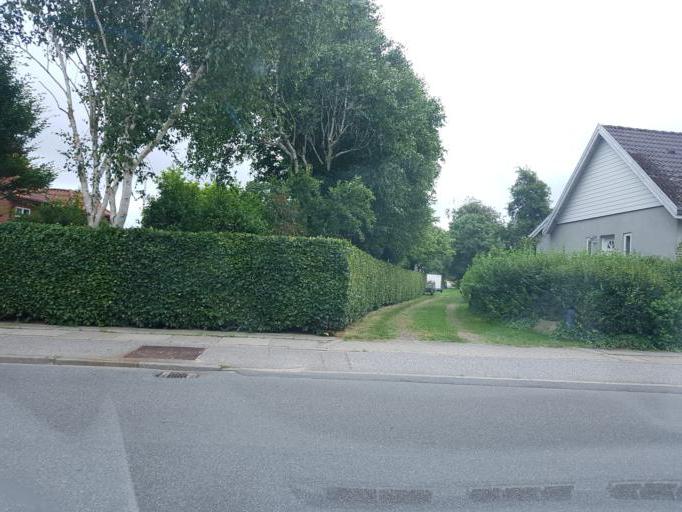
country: DK
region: South Denmark
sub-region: Varde Kommune
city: Varde
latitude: 55.6263
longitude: 8.4861
